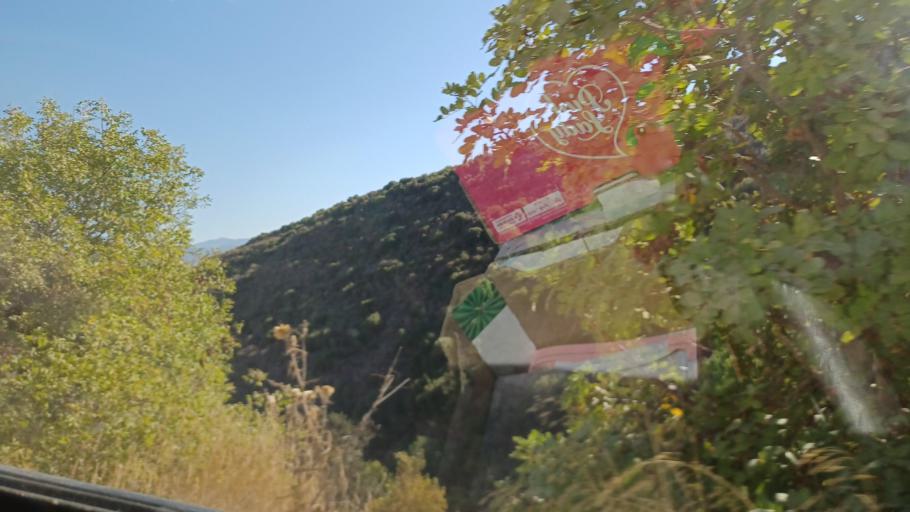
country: CY
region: Pafos
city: Polis
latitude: 34.9644
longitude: 32.4351
